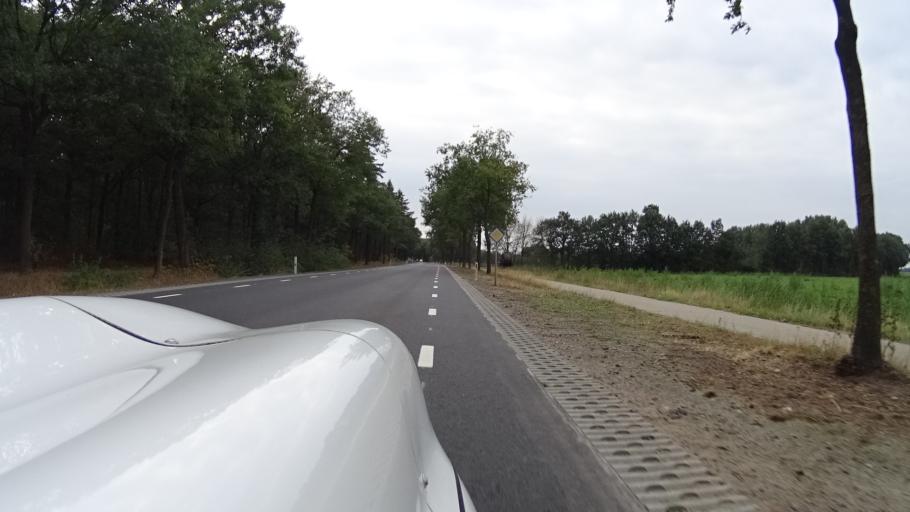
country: NL
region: North Brabant
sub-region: Gemeente Boekel
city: Boekel
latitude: 51.5780
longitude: 5.6490
